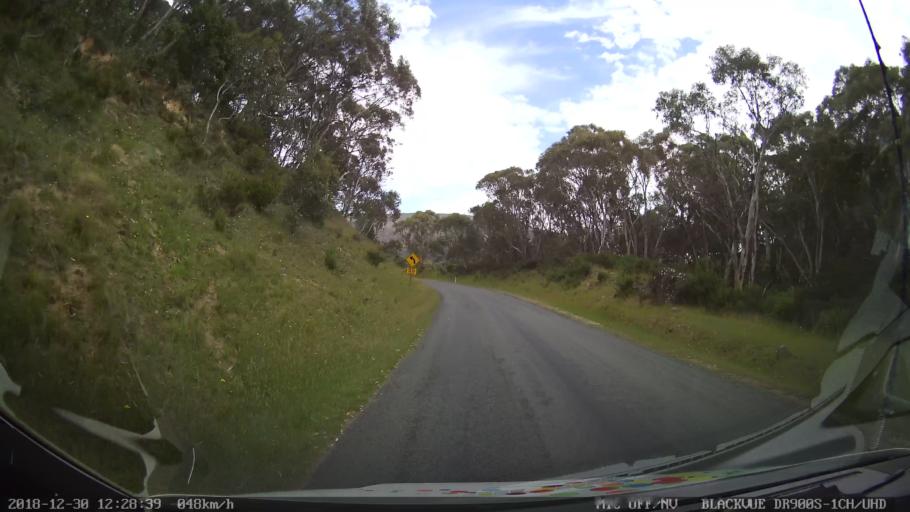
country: AU
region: New South Wales
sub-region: Snowy River
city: Jindabyne
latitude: -36.3247
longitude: 148.4836
